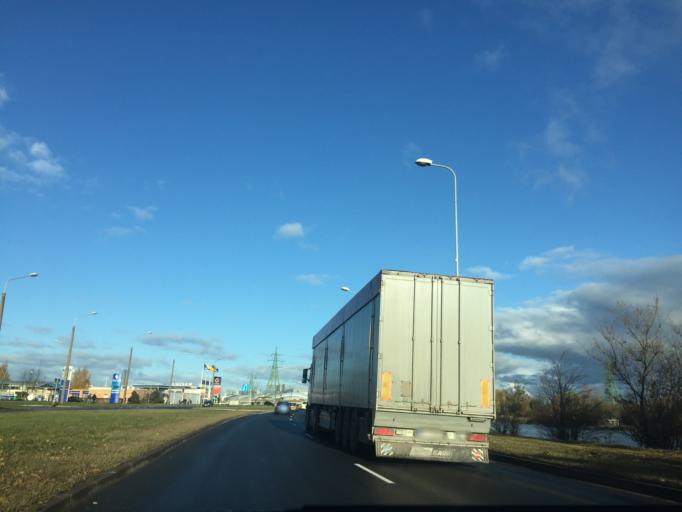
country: LV
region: Riga
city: Riga
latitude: 56.9205
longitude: 24.1106
